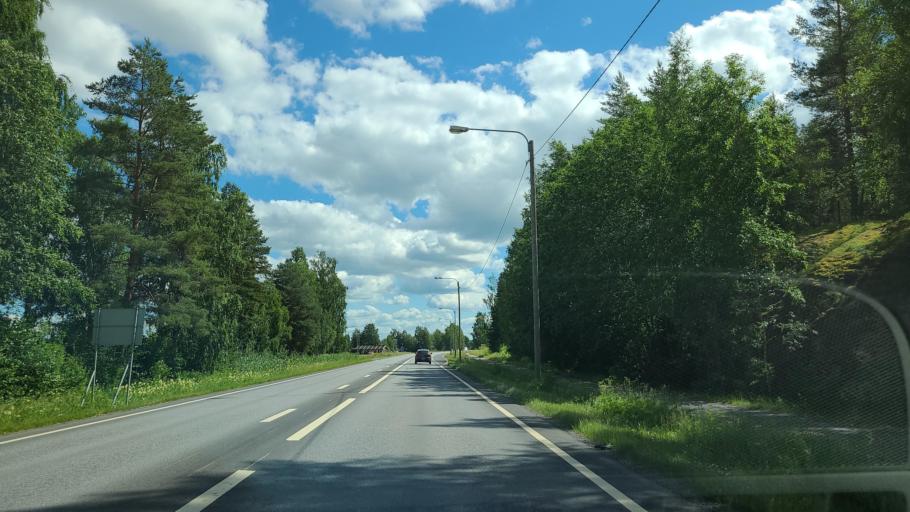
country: FI
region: Ostrobothnia
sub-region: Kyroenmaa
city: Isokyroe
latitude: 62.9741
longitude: 22.3743
